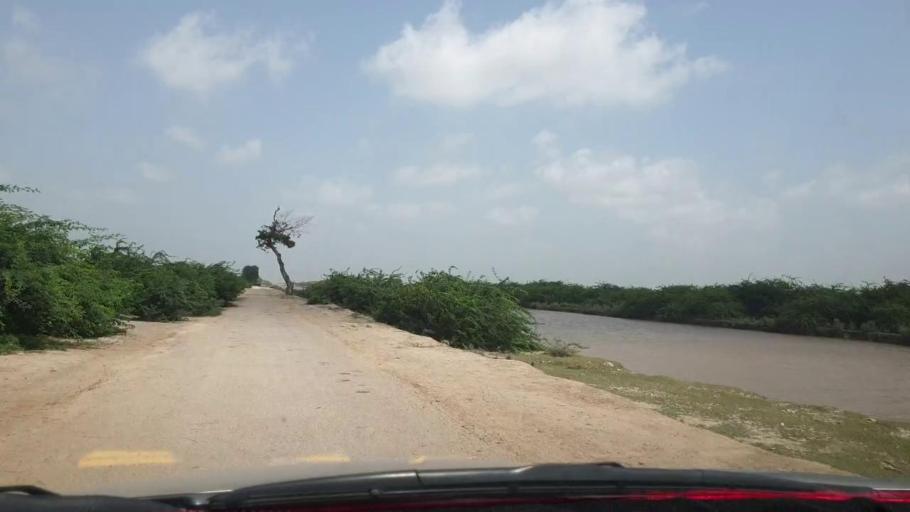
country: PK
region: Sindh
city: Talhar
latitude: 24.8921
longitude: 68.8353
